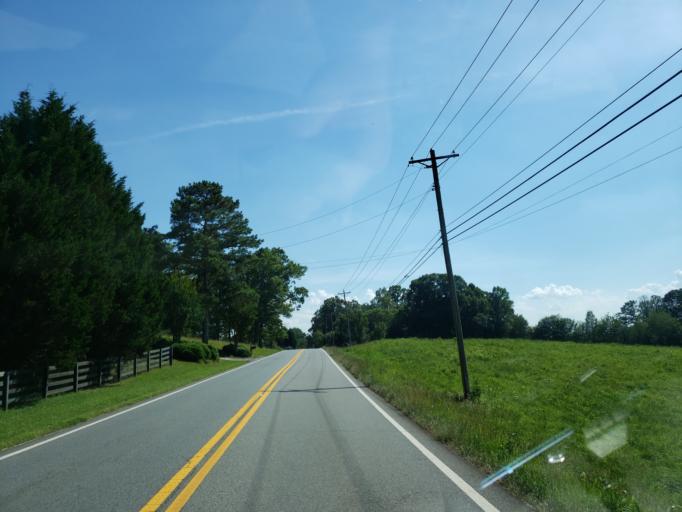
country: US
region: Georgia
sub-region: Cherokee County
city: Woodstock
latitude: 34.1148
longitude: -84.4245
